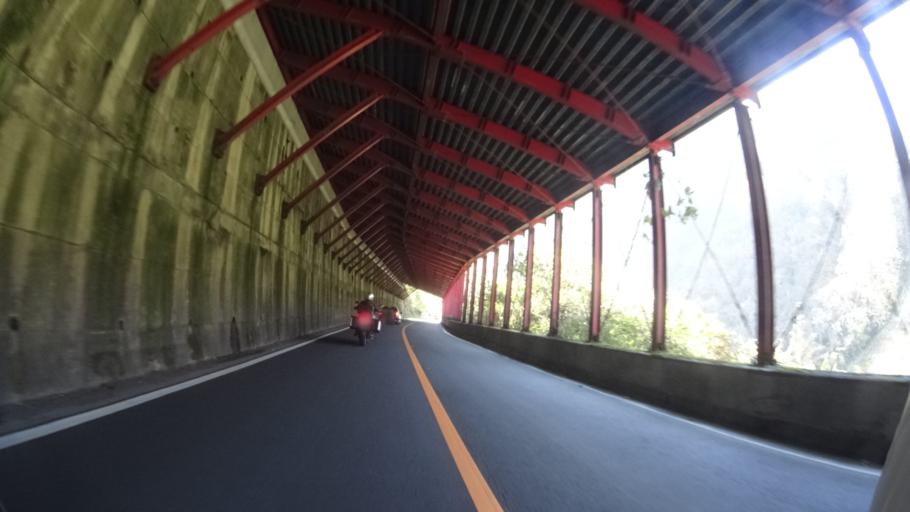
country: JP
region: Fukui
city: Ono
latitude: 35.9396
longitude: 136.6369
